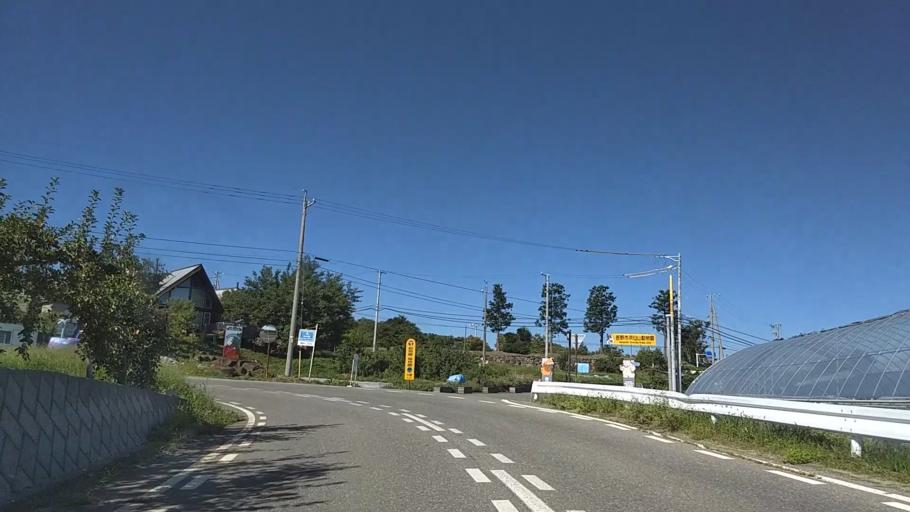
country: JP
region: Nagano
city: Nagano-shi
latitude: 36.5824
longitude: 138.1127
